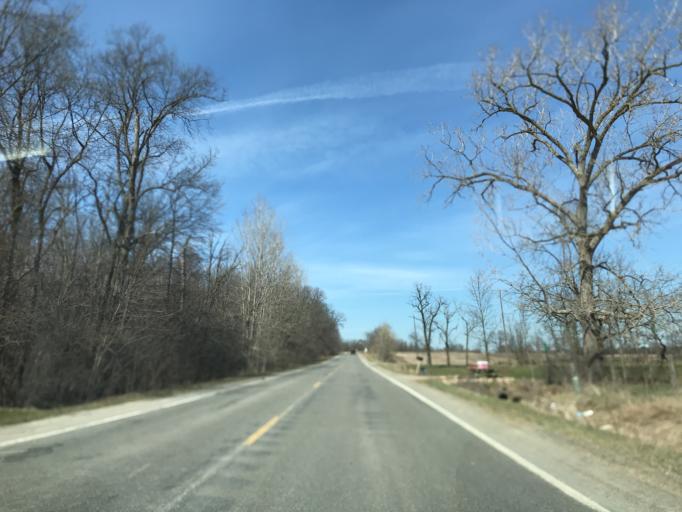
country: US
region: Michigan
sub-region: Washtenaw County
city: Ann Arbor
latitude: 42.3356
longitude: -83.7083
